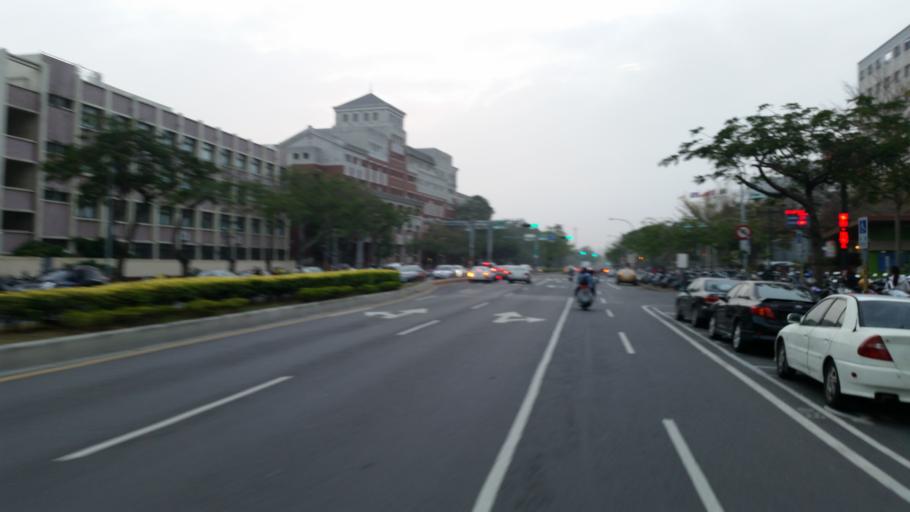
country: TW
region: Taiwan
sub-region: Tainan
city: Tainan
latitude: 23.0010
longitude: 120.2196
